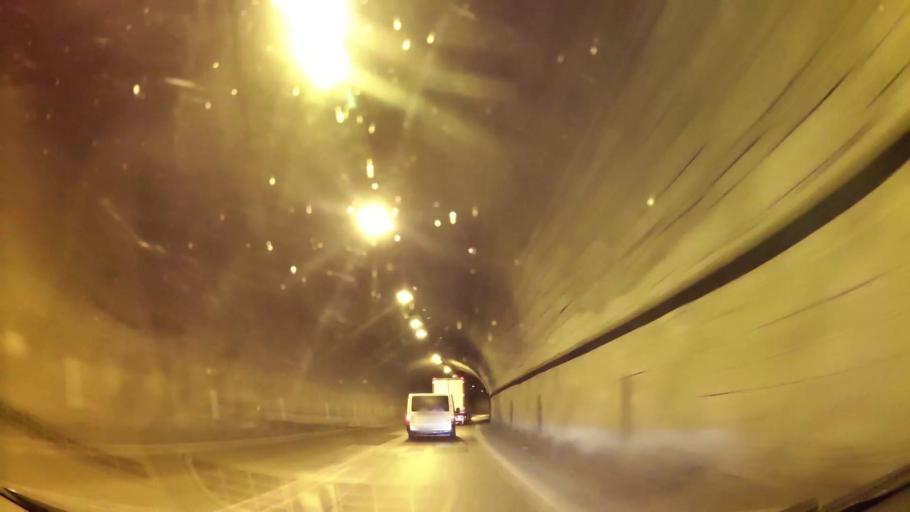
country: RS
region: Central Serbia
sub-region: Pcinjski Okrug
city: Vladicin Han
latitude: 42.7255
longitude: 22.0678
